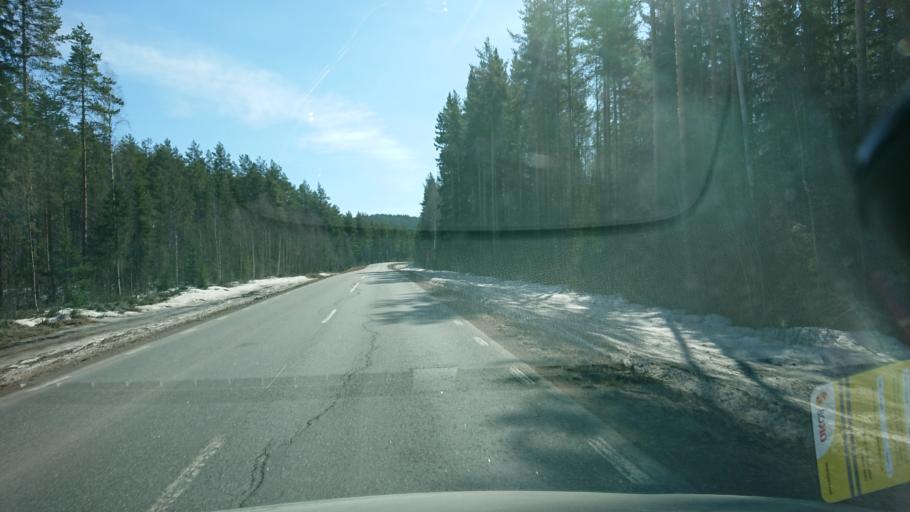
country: SE
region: Vaesternorrland
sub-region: Solleftea Kommun
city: As
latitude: 63.5704
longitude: 16.4503
